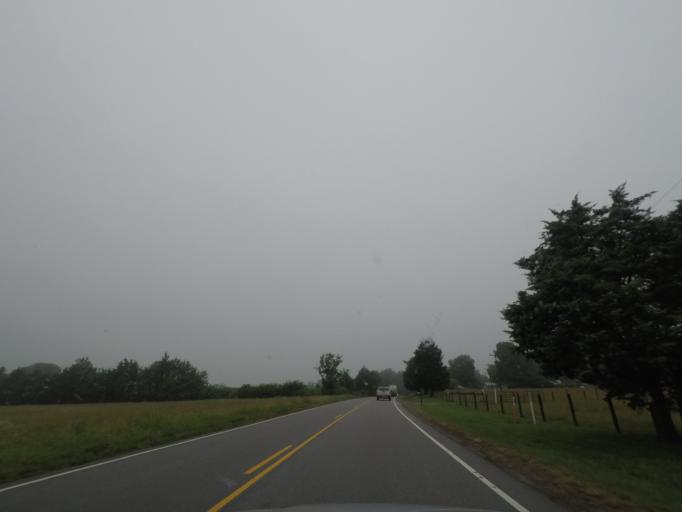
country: US
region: Virginia
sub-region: Prince Edward County
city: Farmville
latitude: 37.3642
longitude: -78.4853
